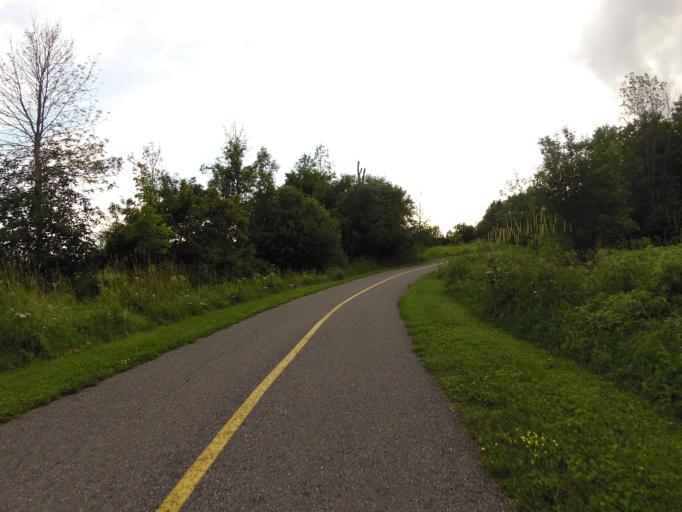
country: CA
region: Ontario
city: Bells Corners
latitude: 45.3331
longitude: -75.8869
